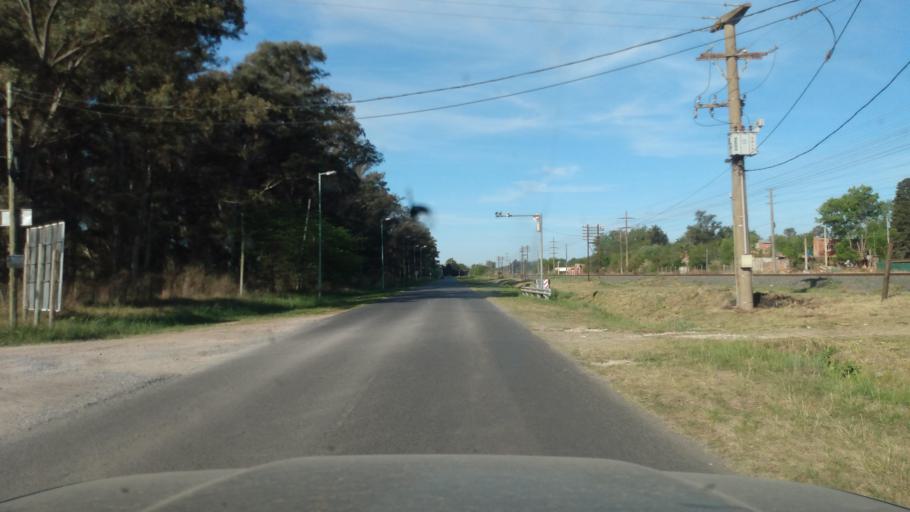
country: AR
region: Buenos Aires
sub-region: Partido de Lujan
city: Lujan
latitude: -34.5878
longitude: -59.1358
